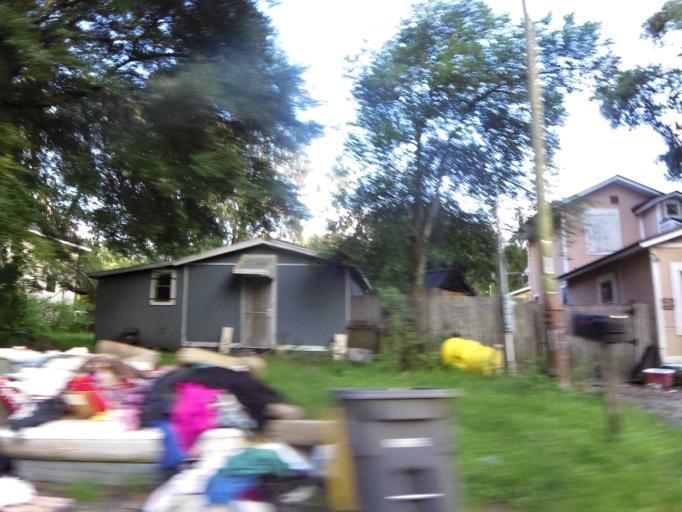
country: US
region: Florida
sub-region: Duval County
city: Jacksonville
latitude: 30.3347
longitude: -81.7031
